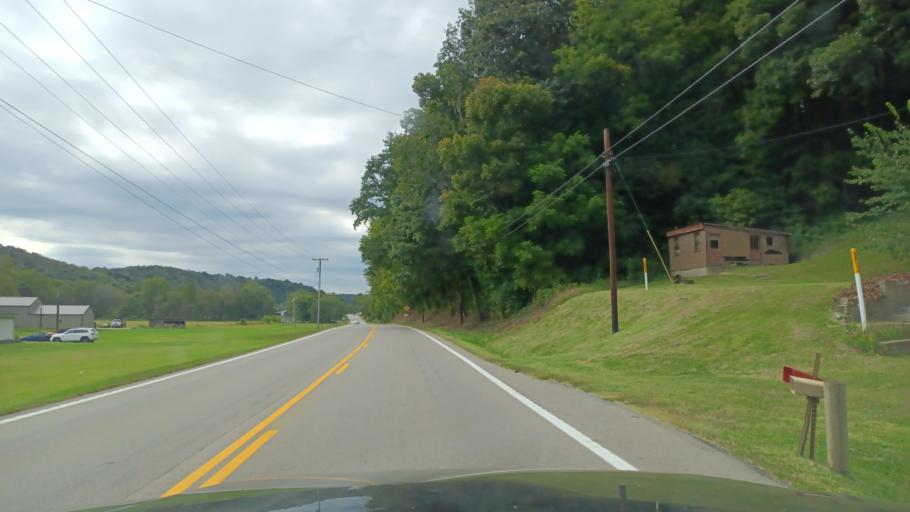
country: US
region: Ohio
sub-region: Vinton County
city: McArthur
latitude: 39.2722
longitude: -82.5988
